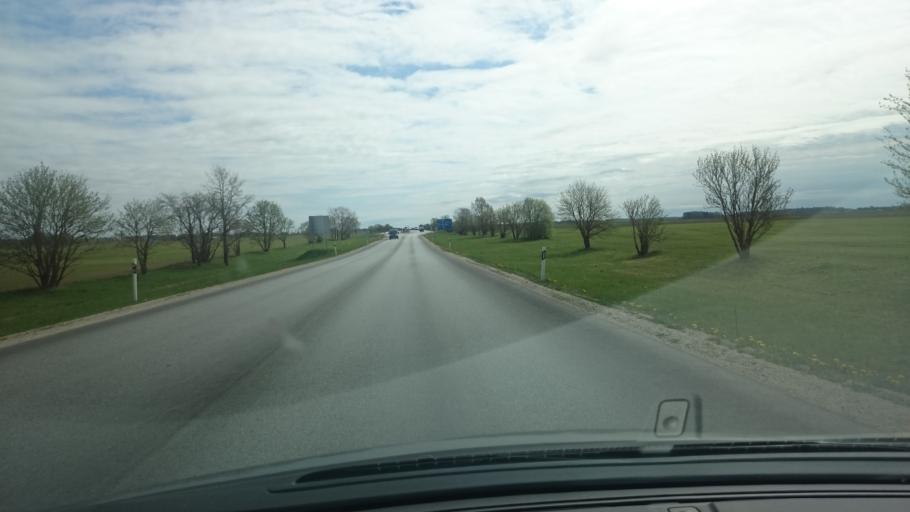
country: EE
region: Laeaene-Virumaa
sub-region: Haljala vald
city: Haljala
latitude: 59.4273
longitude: 26.2399
